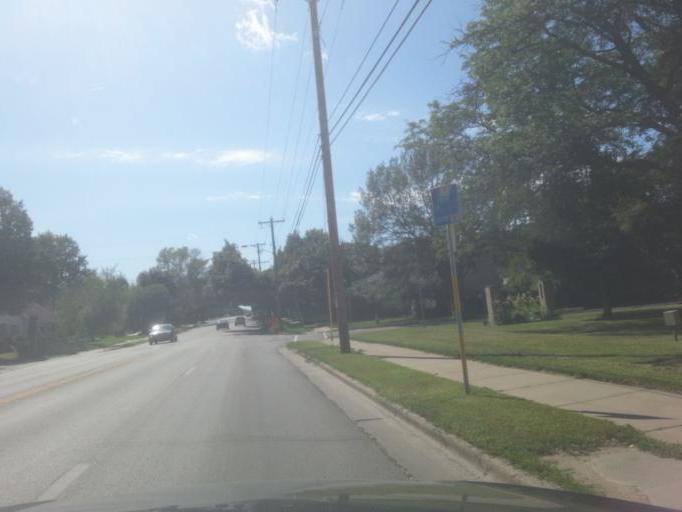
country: US
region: Wisconsin
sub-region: Dane County
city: Shorewood Hills
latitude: 43.0608
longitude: -89.4408
